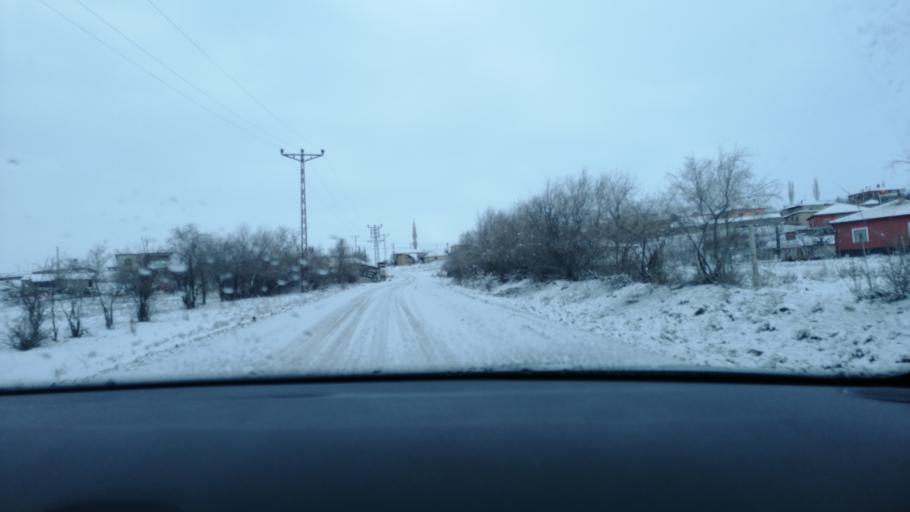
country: TR
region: Aksaray
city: Agacoren
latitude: 38.9368
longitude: 33.9484
